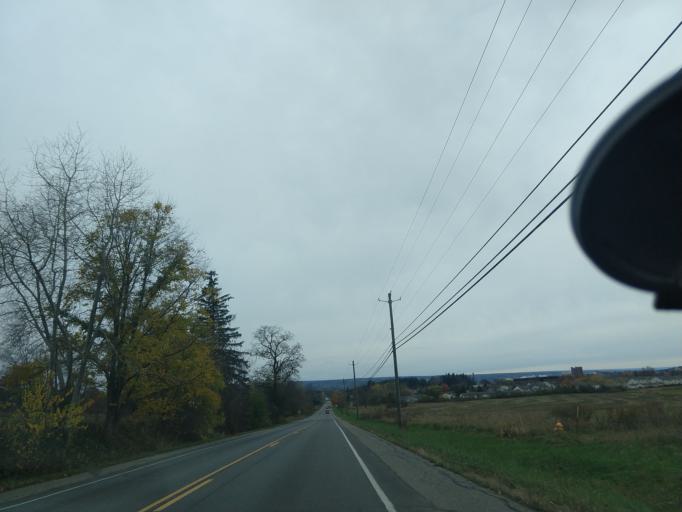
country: US
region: New York
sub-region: Tompkins County
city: East Ithaca
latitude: 42.4343
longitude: -76.4545
